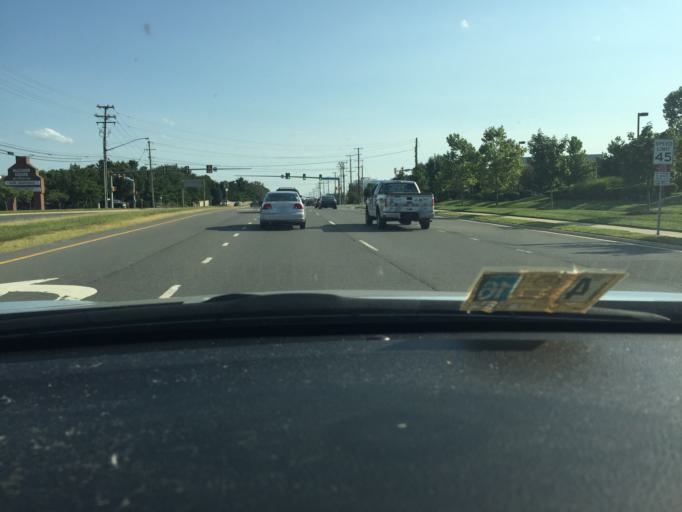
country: US
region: Virginia
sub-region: Fairfax County
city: Floris
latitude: 38.9223
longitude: -77.4176
